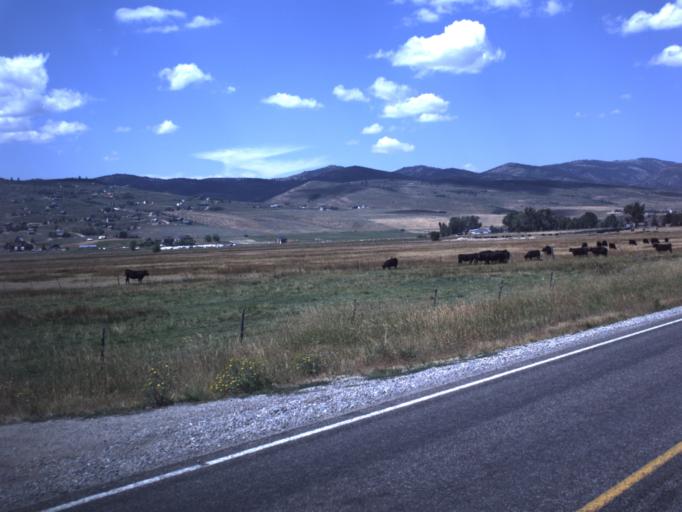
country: US
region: Utah
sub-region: Rich County
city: Randolph
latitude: 41.9032
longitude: -111.3745
